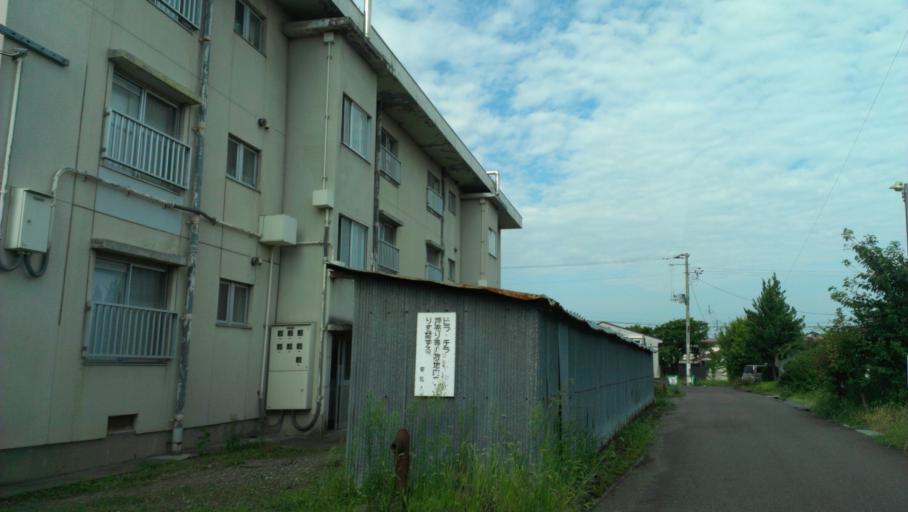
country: JP
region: Fukushima
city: Kitakata
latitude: 37.4946
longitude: 139.9172
